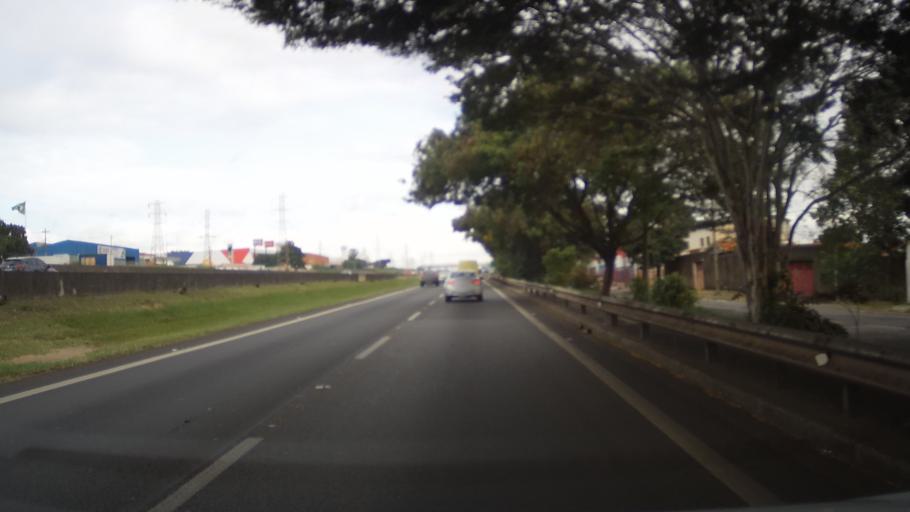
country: BR
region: Sao Paulo
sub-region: Campinas
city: Campinas
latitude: -22.9253
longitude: -47.0865
